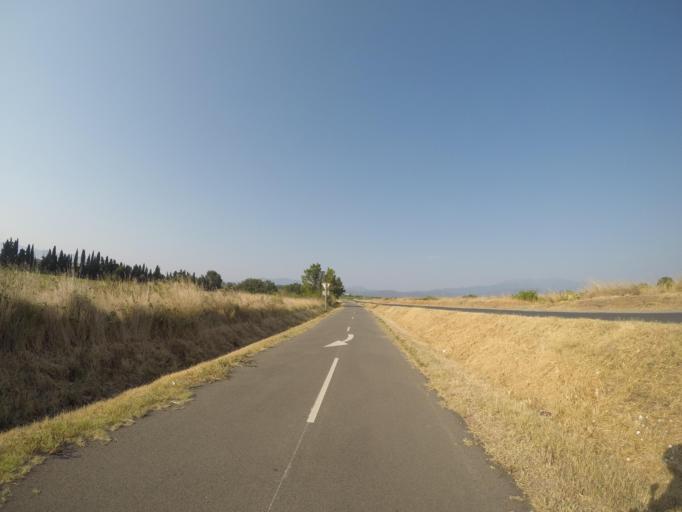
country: FR
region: Languedoc-Roussillon
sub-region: Departement des Pyrenees-Orientales
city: Ponteilla
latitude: 42.6344
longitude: 2.8080
